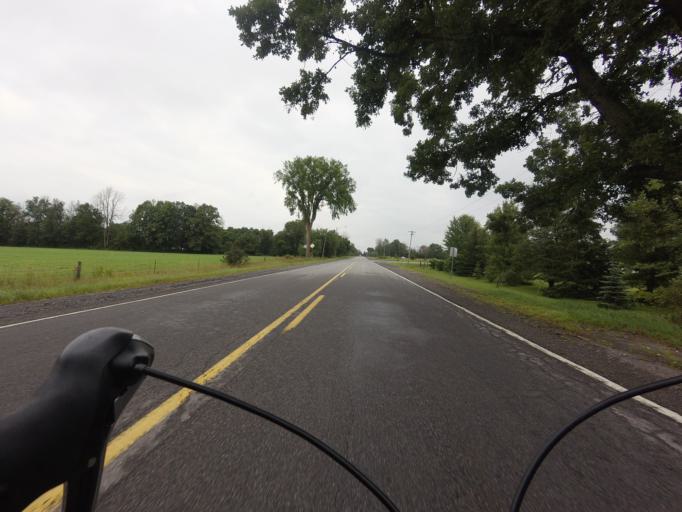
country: CA
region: Ontario
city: Bells Corners
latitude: 45.1624
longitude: -75.7986
